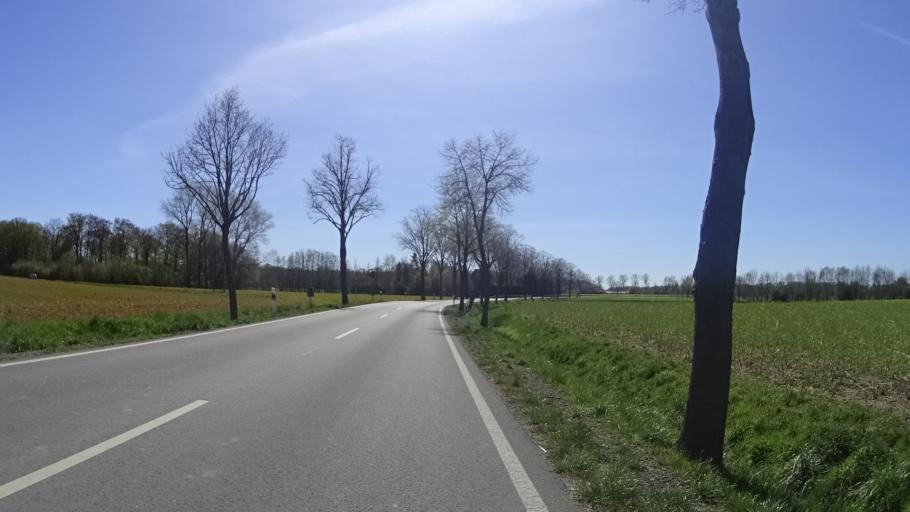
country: DE
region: North Rhine-Westphalia
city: Ludinghausen
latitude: 51.8301
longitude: 7.3997
